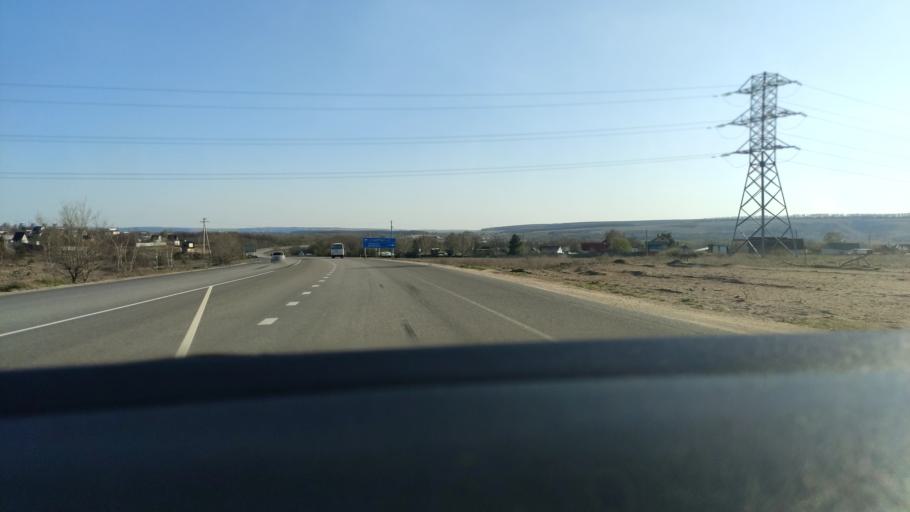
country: RU
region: Voronezj
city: Kolodeznyy
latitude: 51.3514
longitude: 39.1734
